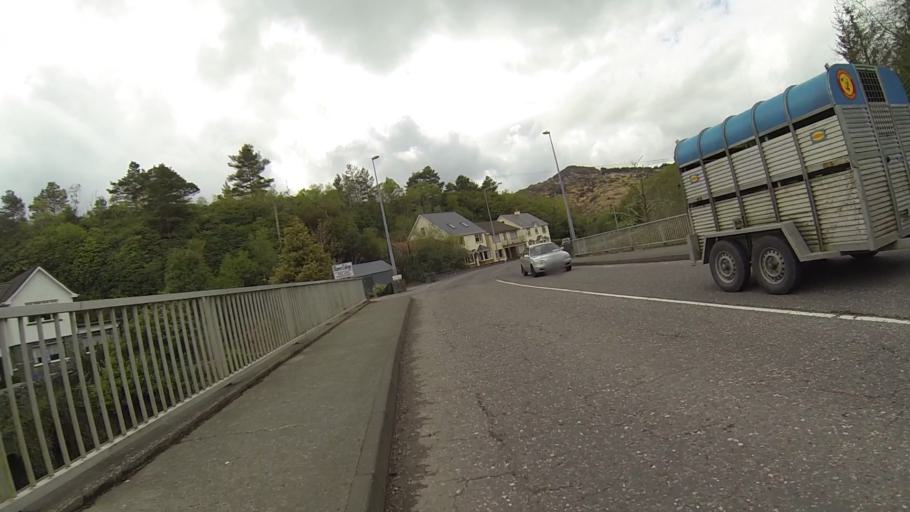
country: IE
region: Munster
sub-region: County Cork
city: Bantry
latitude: 51.7492
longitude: -9.5532
